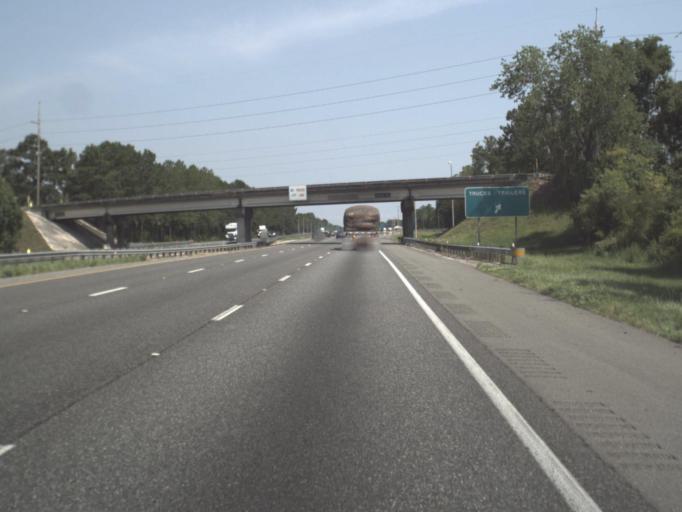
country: US
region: Florida
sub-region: Hamilton County
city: Jasper
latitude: 30.4076
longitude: -82.8905
